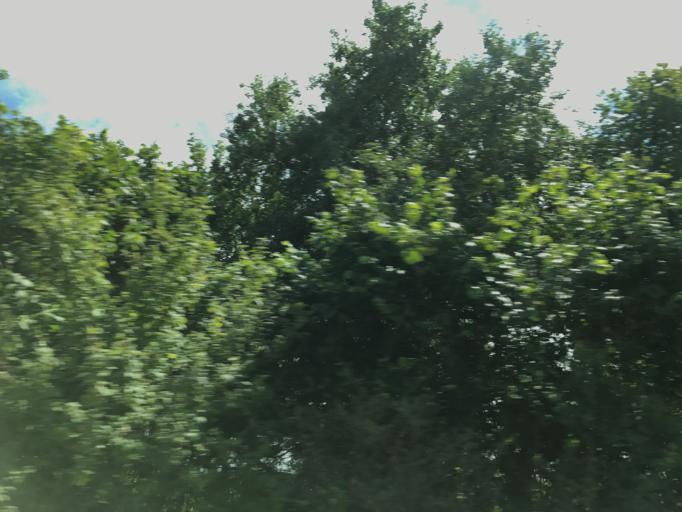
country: DE
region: Baden-Wuerttemberg
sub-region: Tuebingen Region
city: Ertingen
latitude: 48.0988
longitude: 9.4439
